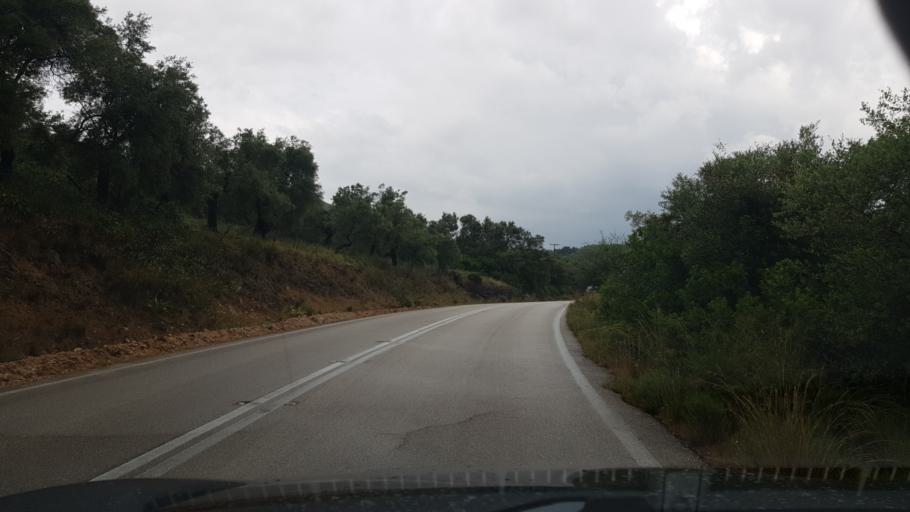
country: GR
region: Ionian Islands
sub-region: Lefkada
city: Nidri
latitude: 38.6418
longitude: 20.6752
